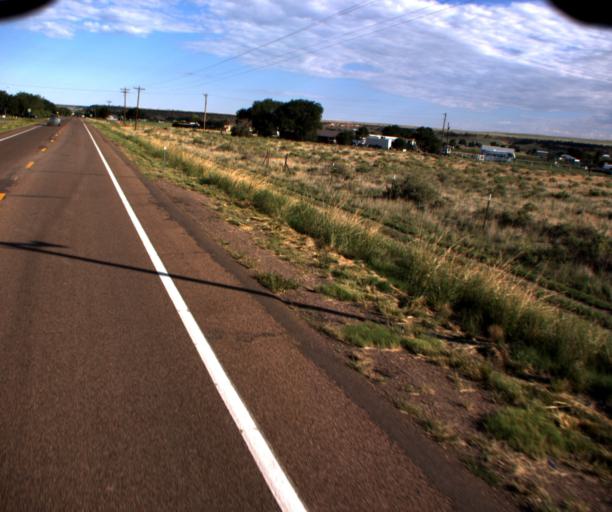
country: US
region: Arizona
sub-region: Apache County
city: Springerville
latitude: 34.1242
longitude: -109.2626
